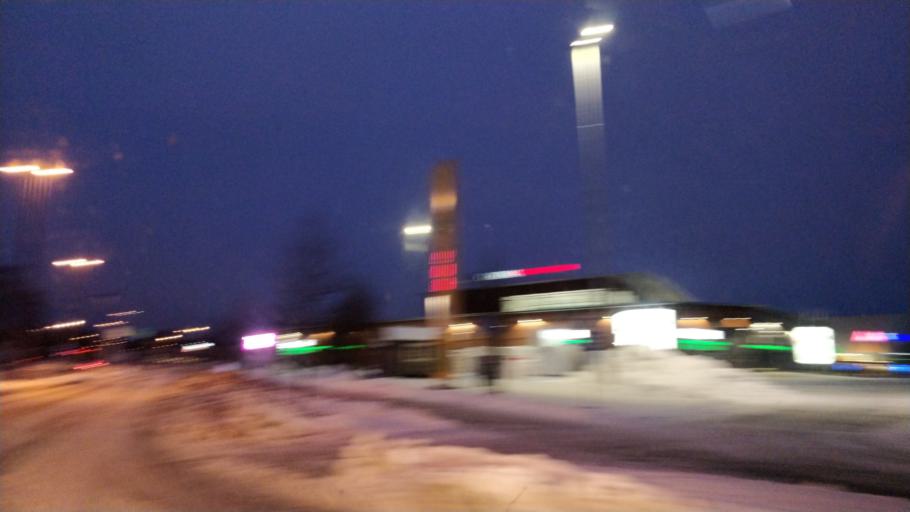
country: FI
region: Lapland
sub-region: Kemi-Tornio
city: Kemi
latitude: 65.7412
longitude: 24.5771
